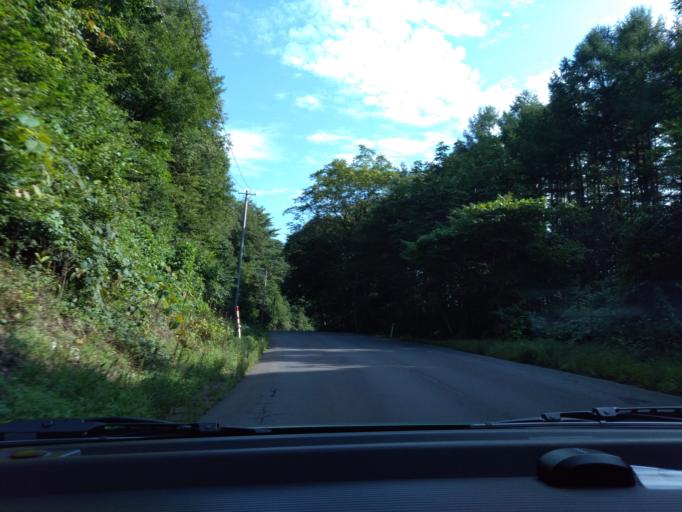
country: JP
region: Iwate
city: Morioka-shi
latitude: 39.5960
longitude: 141.0891
